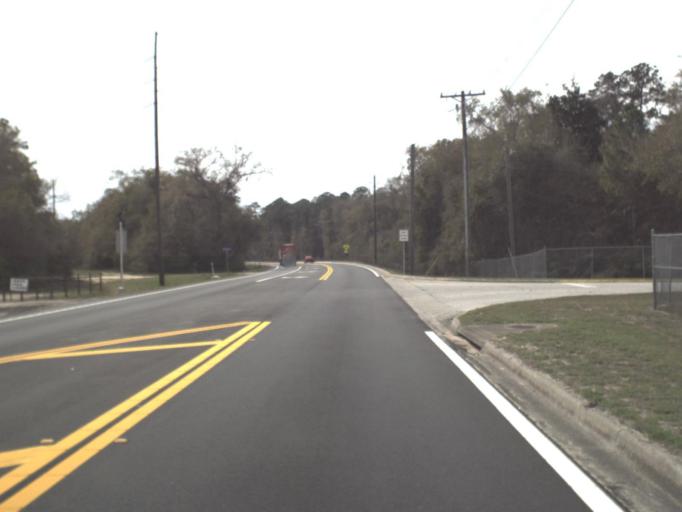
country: US
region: Florida
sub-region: Gadsden County
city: Midway
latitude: 30.4371
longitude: -84.5156
